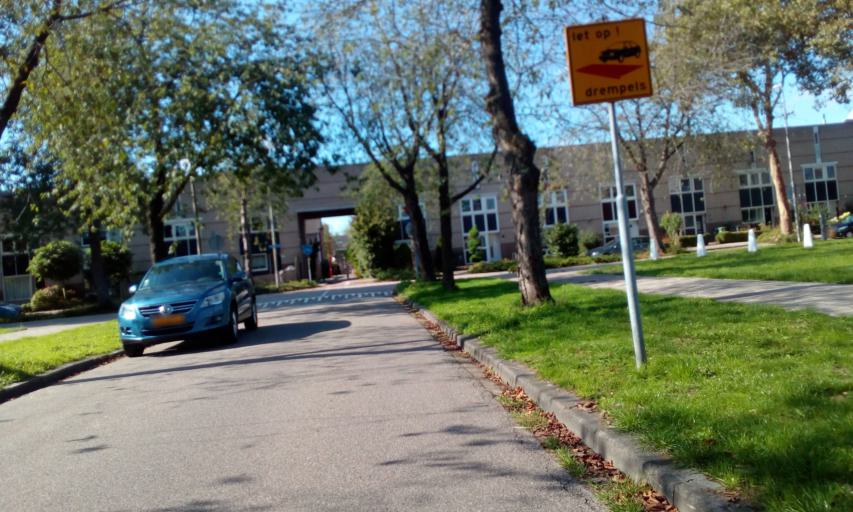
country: NL
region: South Holland
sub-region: Gemeente Zoetermeer
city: Zoetermeer
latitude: 52.0728
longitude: 4.5158
